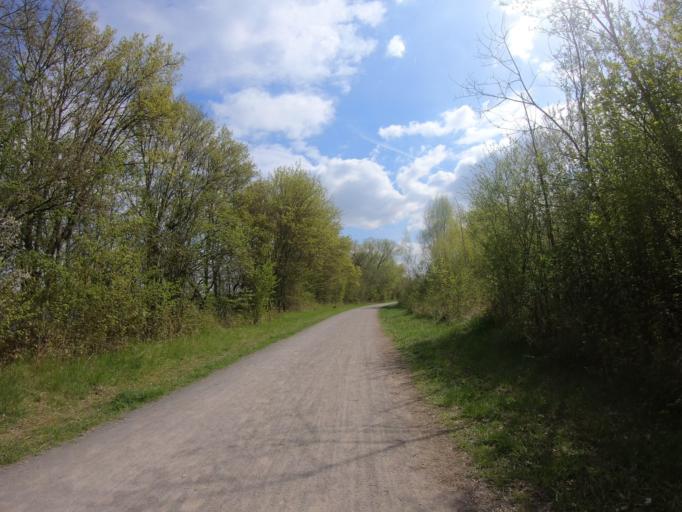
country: DE
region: Lower Saxony
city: Laatzen
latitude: 52.2747
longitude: 9.8087
